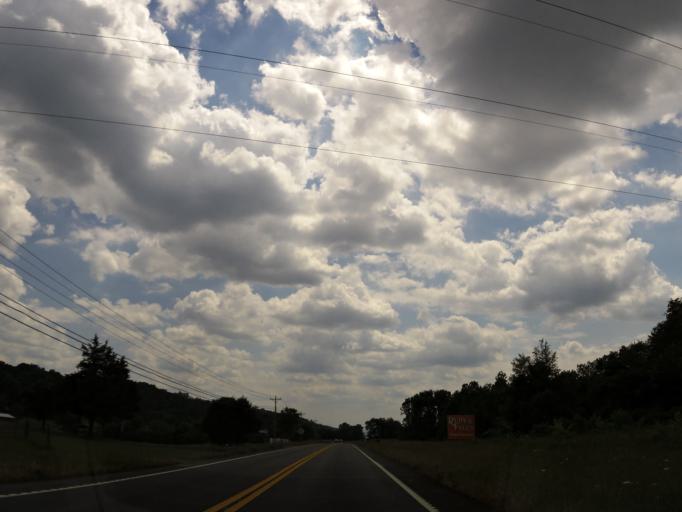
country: US
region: Tennessee
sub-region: Bledsoe County
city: Pikeville
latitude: 35.5092
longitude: -85.2851
